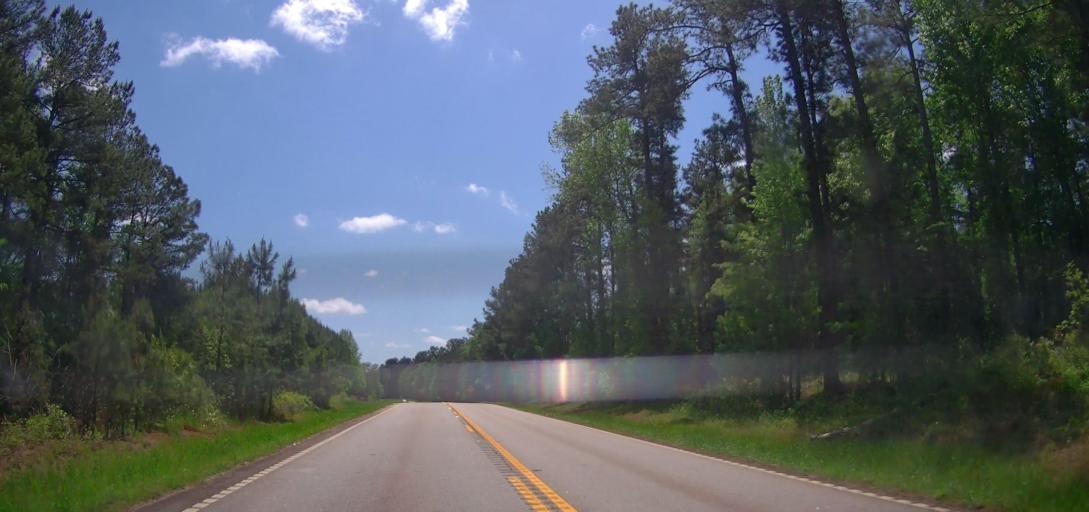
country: US
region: Georgia
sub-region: Jasper County
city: Monticello
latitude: 33.1593
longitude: -83.6410
